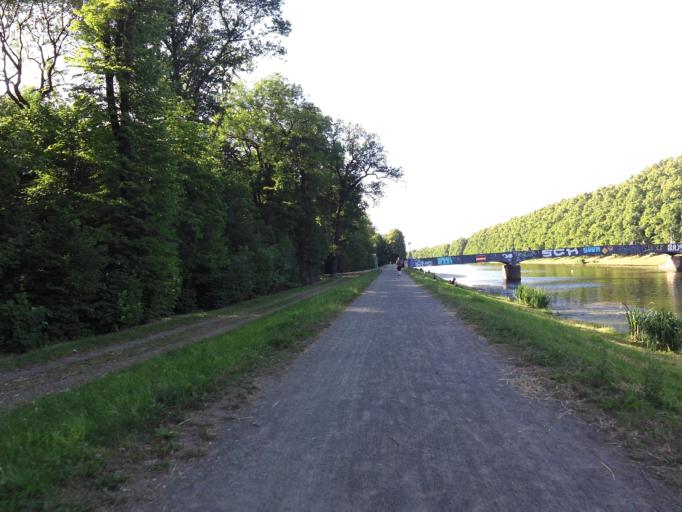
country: DE
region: Saxony
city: Leipzig
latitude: 51.3254
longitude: 12.3561
